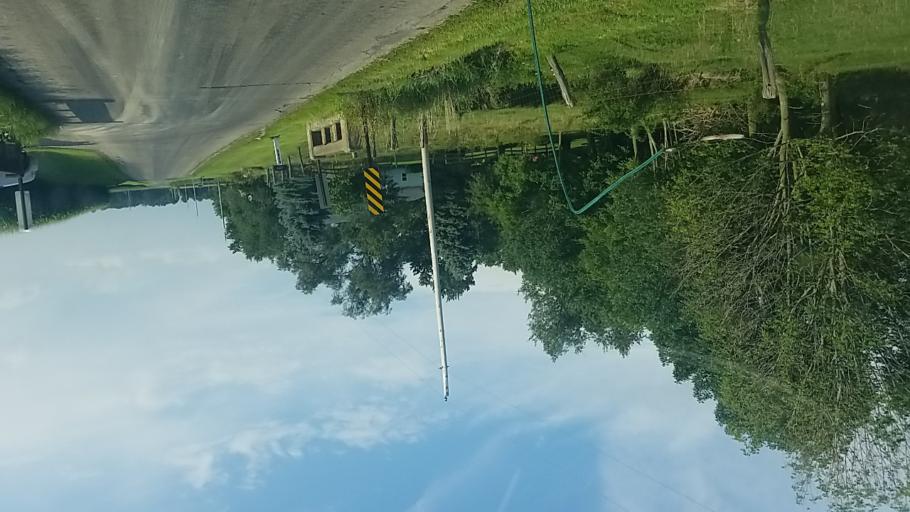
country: US
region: Ohio
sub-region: Wayne County
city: West Salem
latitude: 40.8776
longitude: -82.0737
